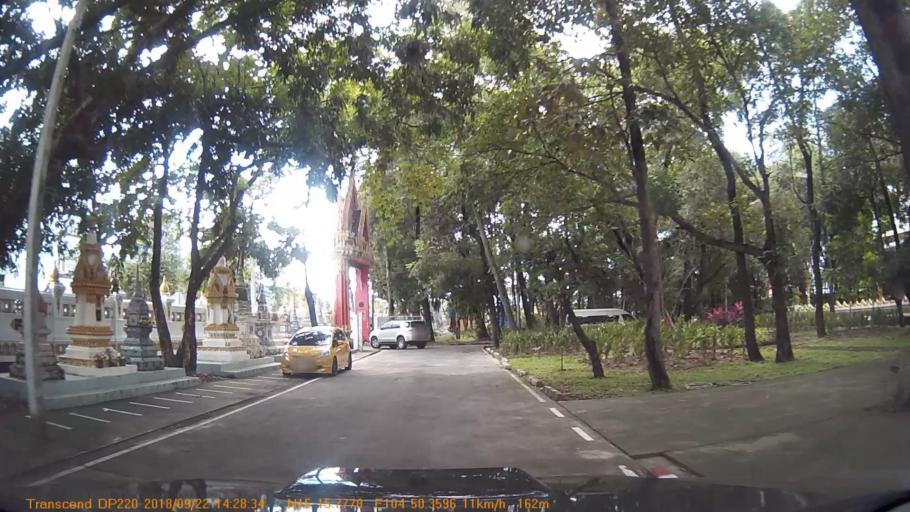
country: TH
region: Changwat Ubon Ratchathani
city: Ubon Ratchathani
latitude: 15.2629
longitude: 104.8392
